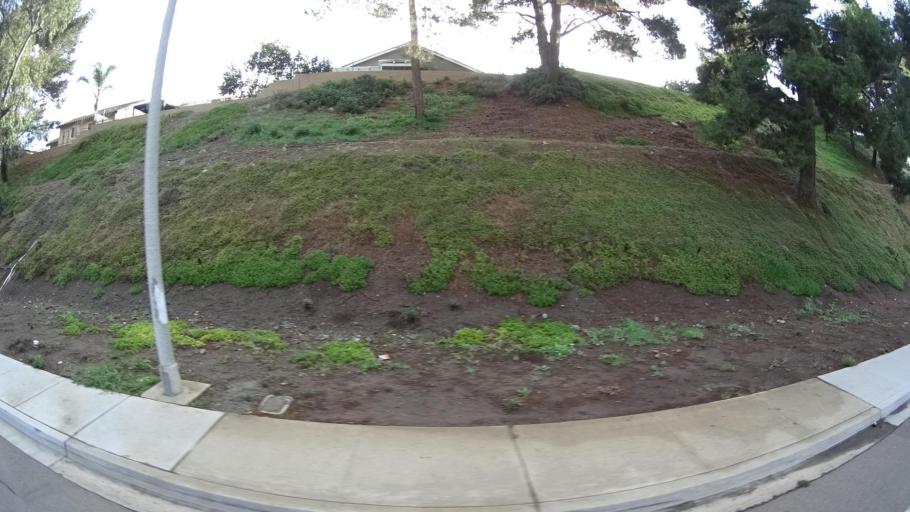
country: US
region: California
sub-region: San Diego County
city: Spring Valley
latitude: 32.7321
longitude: -116.9715
